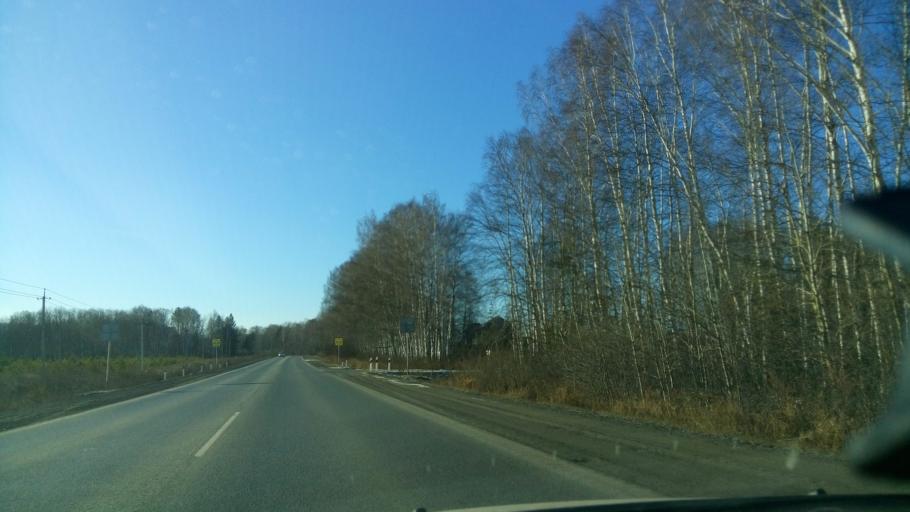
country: RU
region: Sverdlovsk
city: Gornyy Shchit
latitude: 56.6631
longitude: 60.4351
